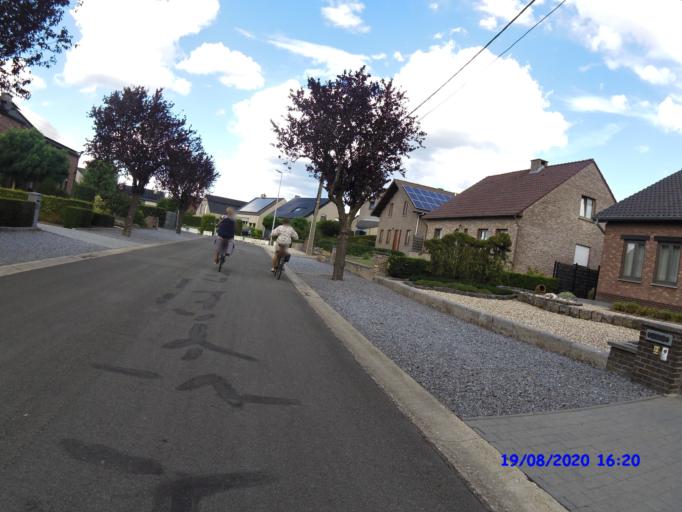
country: BE
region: Flanders
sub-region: Provincie Limburg
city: Nieuwerkerken
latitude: 50.8618
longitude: 5.1984
